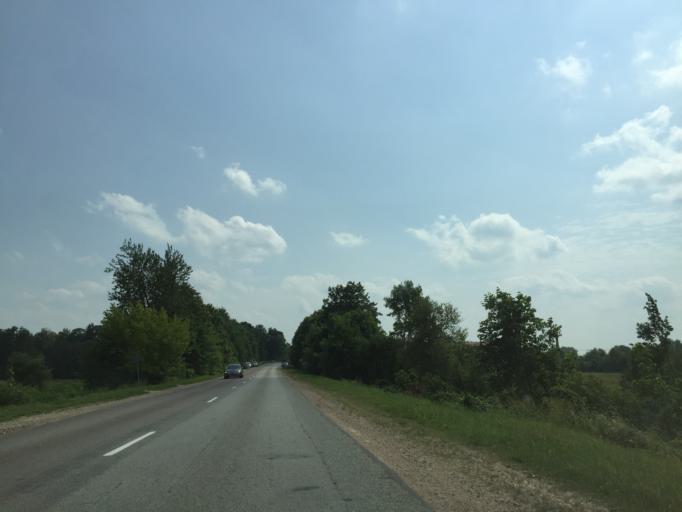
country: LV
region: Jelgava
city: Jelgava
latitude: 56.6912
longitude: 23.7190
